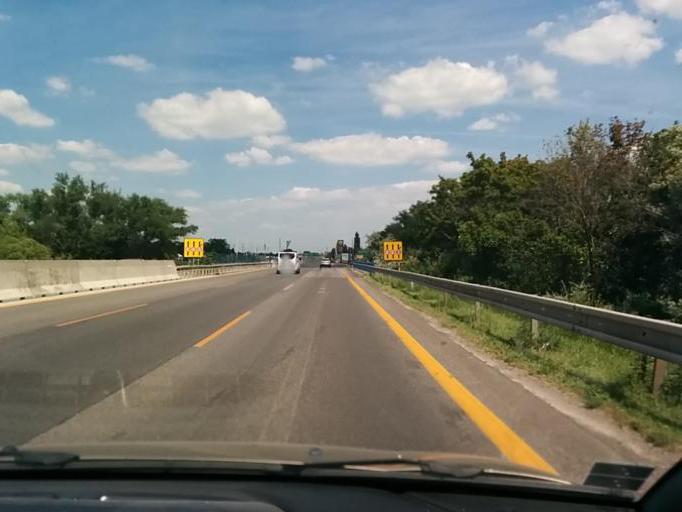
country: SK
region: Trnavsky
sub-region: Okres Trnava
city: Trnava
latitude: 48.3239
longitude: 17.6049
